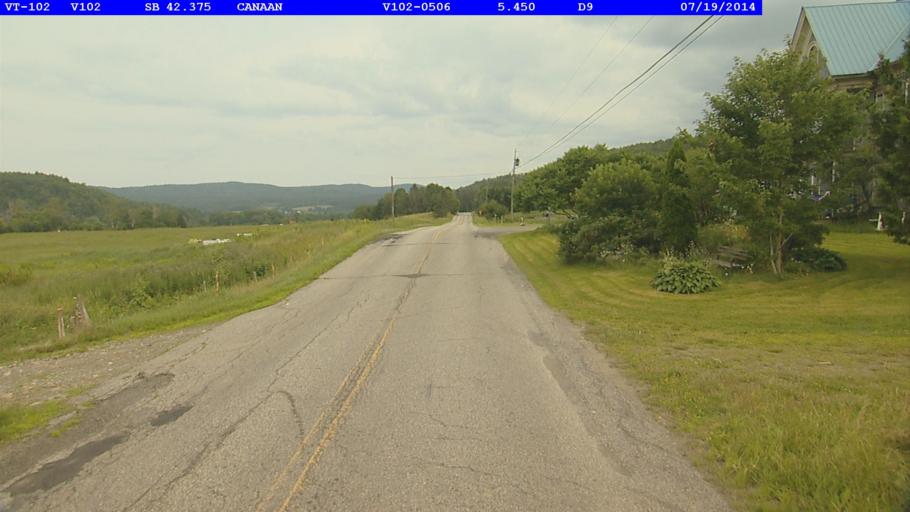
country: US
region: New Hampshire
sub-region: Coos County
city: Colebrook
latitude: 44.9778
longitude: -71.5406
